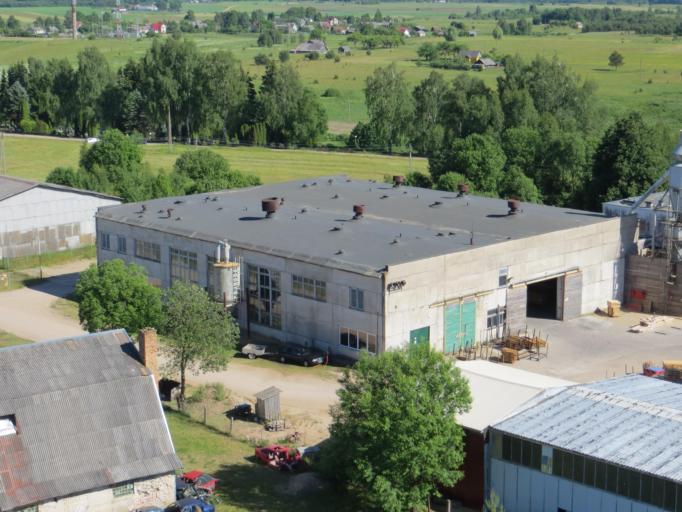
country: LT
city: Moletai
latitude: 55.0753
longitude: 25.2469
